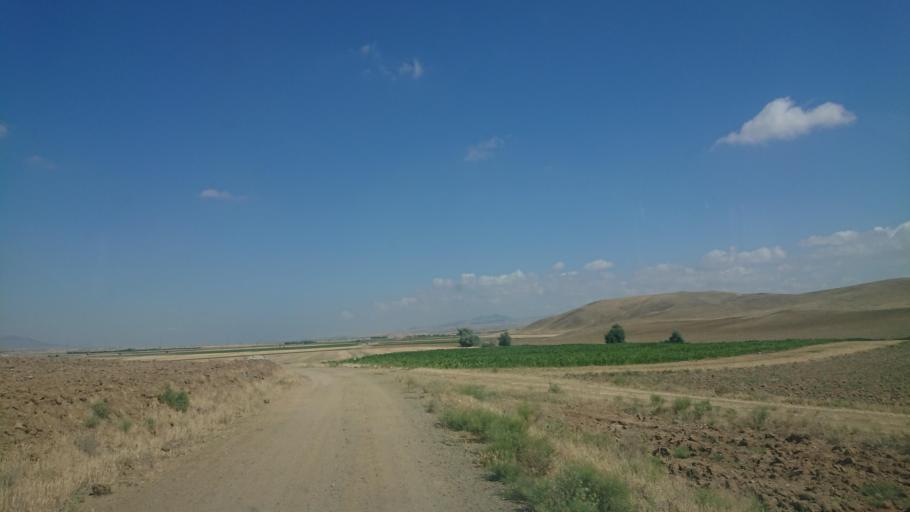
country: TR
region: Aksaray
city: Sariyahsi
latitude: 38.9688
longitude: 33.9201
